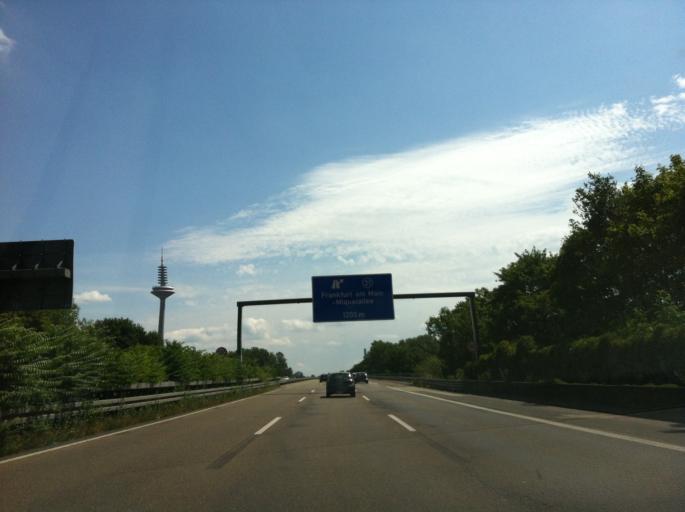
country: DE
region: Hesse
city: Niederrad
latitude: 50.1346
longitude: 8.6321
